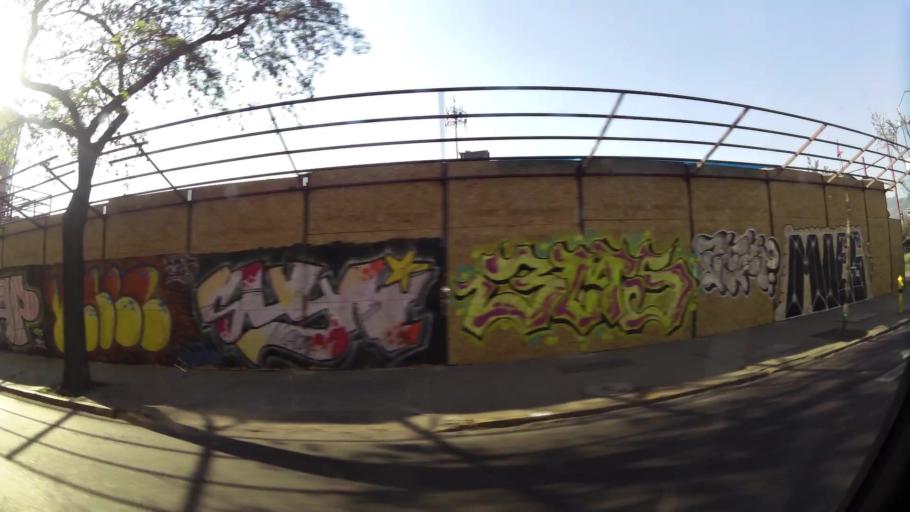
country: CL
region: Santiago Metropolitan
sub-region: Provincia de Santiago
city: Santiago
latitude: -33.4331
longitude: -70.6548
